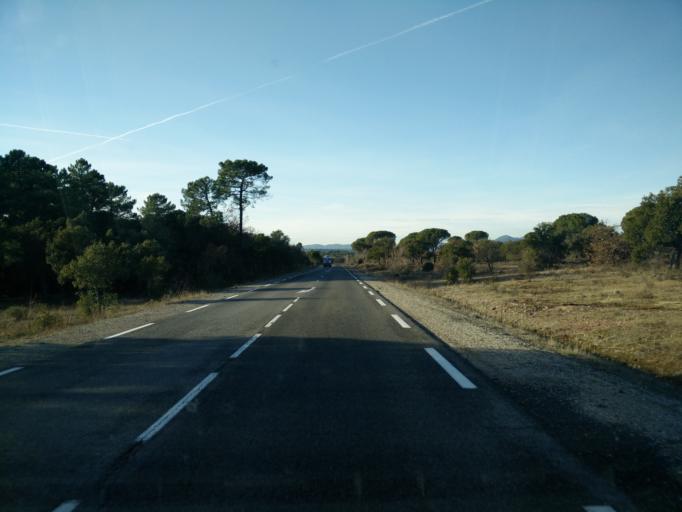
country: FR
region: Provence-Alpes-Cote d'Azur
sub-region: Departement du Var
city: La Garde-Freinet
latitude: 43.3517
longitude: 6.4218
